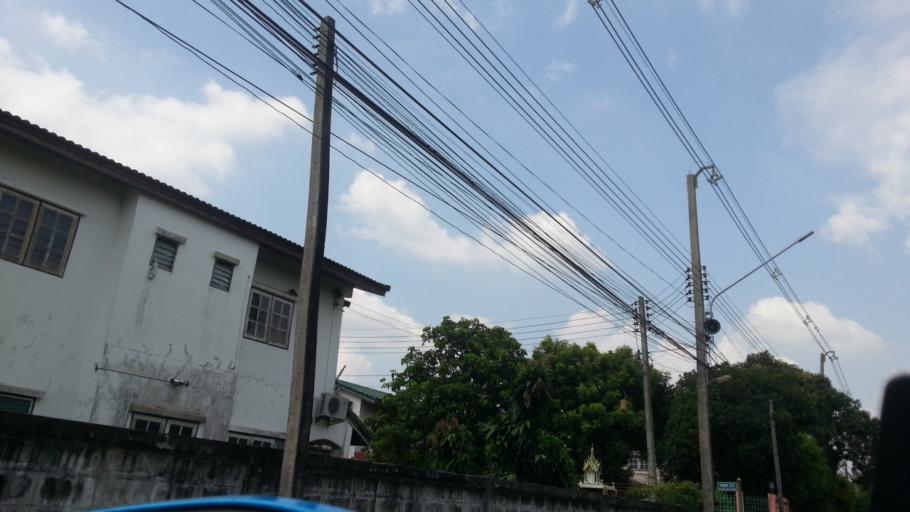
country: TH
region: Pathum Thani
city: Ban Rangsit
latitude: 14.0485
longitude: 100.8312
